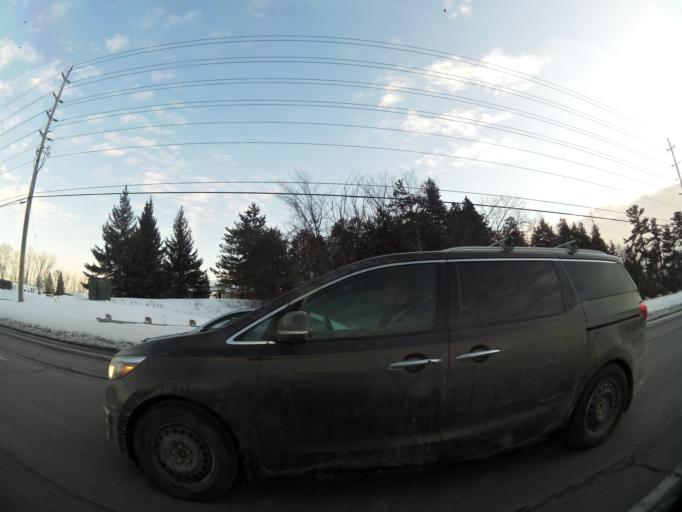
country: CA
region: Ontario
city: Ottawa
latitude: 45.4238
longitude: -75.5835
